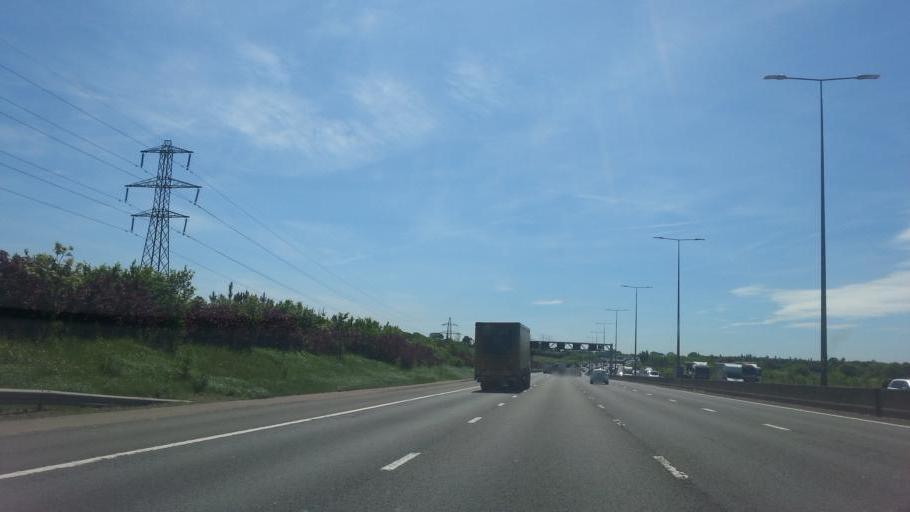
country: GB
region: England
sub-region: Hertfordshire
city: Redbourn
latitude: 51.7933
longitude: -0.4118
